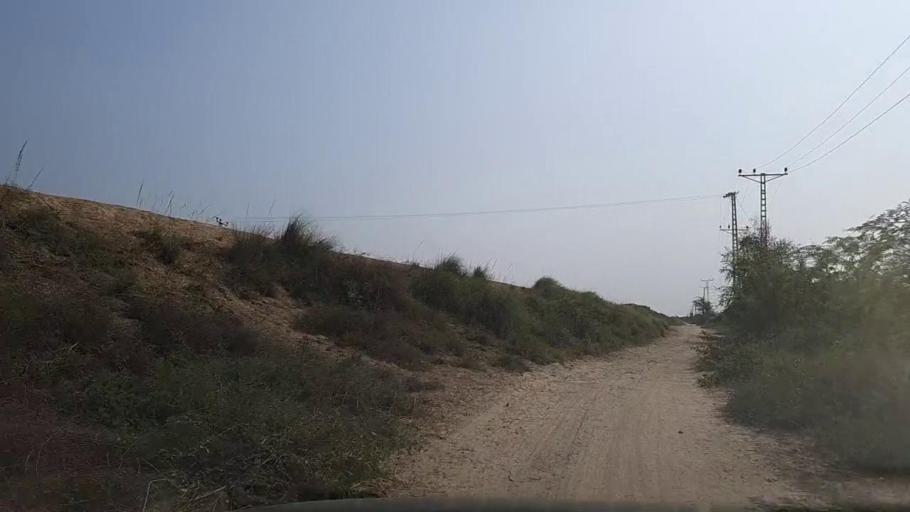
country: PK
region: Sindh
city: Chuhar Jamali
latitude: 24.5519
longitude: 67.9181
